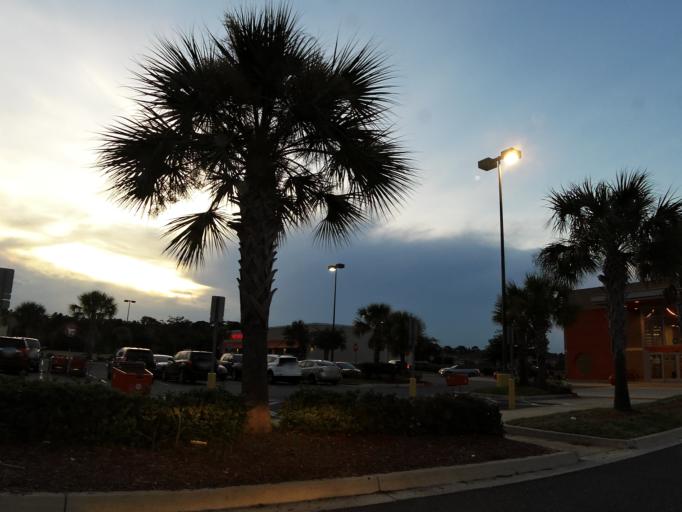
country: US
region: Florida
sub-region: Nassau County
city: Yulee
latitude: 30.6297
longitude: -81.5539
